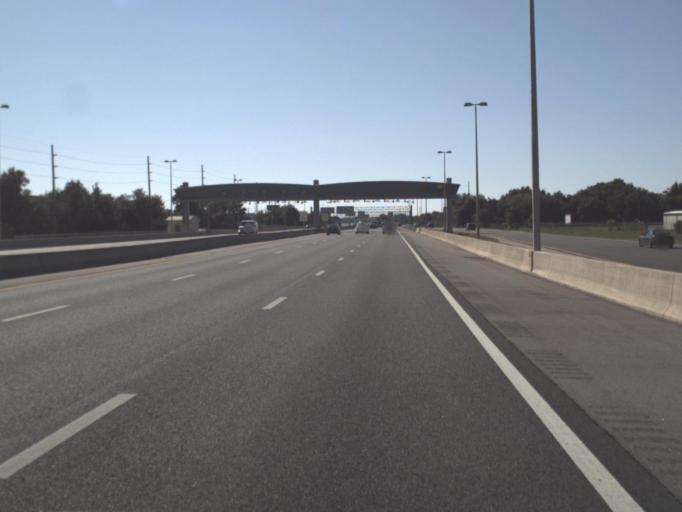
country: US
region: Florida
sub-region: Orange County
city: Sky Lake
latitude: 28.4446
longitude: -81.3831
